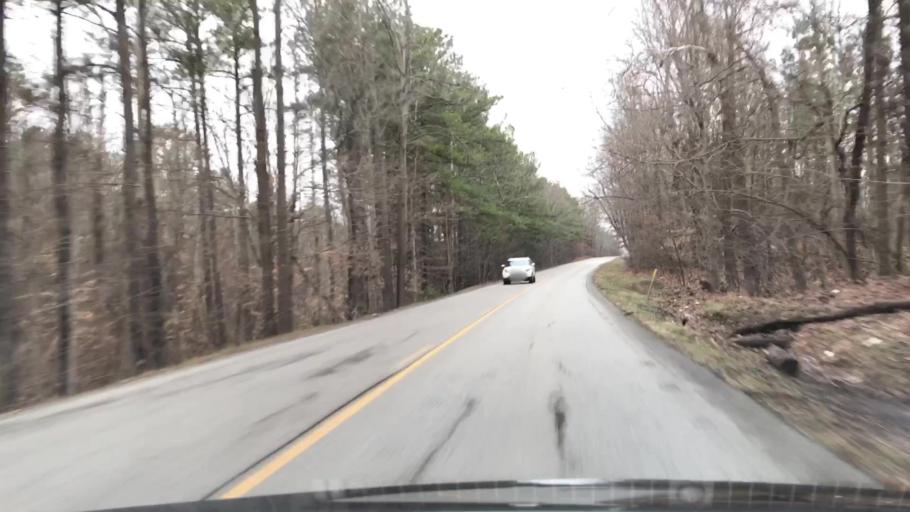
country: US
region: Kentucky
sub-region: Muhlenberg County
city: Morehead
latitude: 37.2862
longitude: -87.2103
